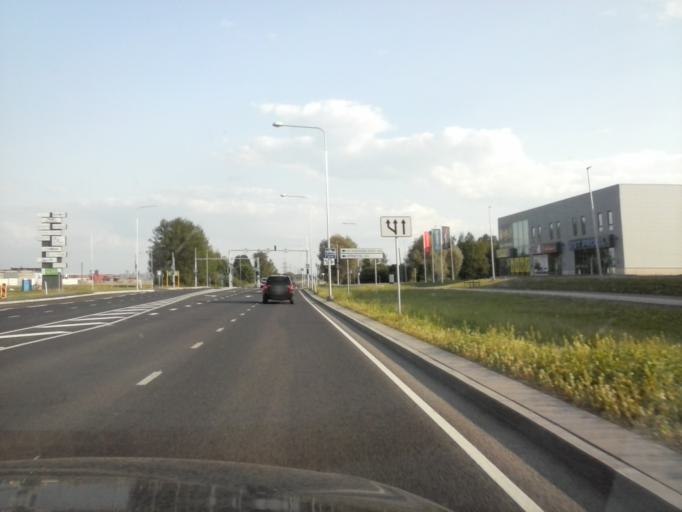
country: EE
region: Tartu
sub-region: Tartu linn
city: Tartu
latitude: 58.3565
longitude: 26.7406
